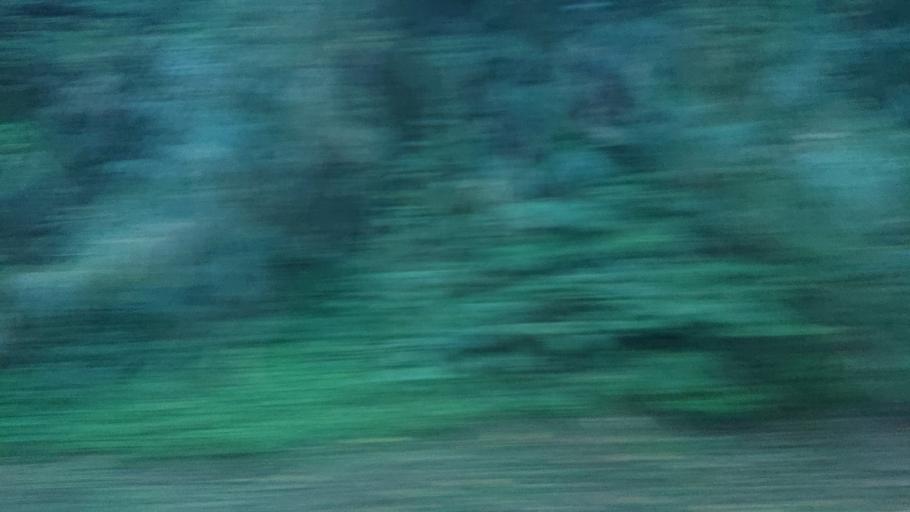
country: TW
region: Taiwan
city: Lugu
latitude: 23.4800
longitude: 120.8330
